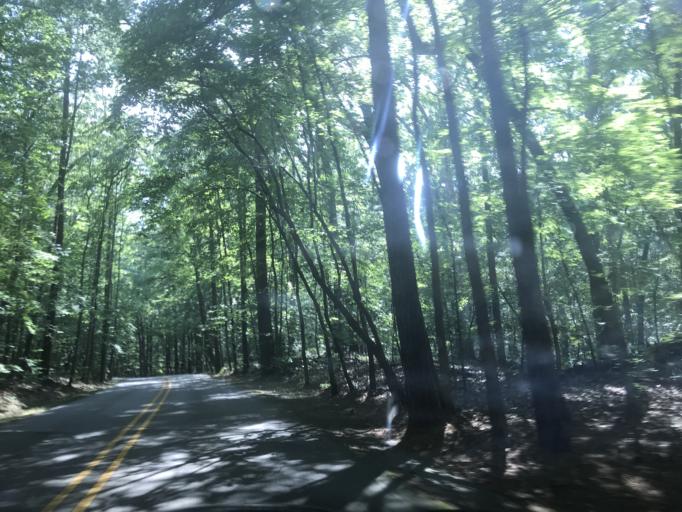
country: US
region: North Carolina
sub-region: Wake County
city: Morrisville
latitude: 35.8884
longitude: -78.7550
